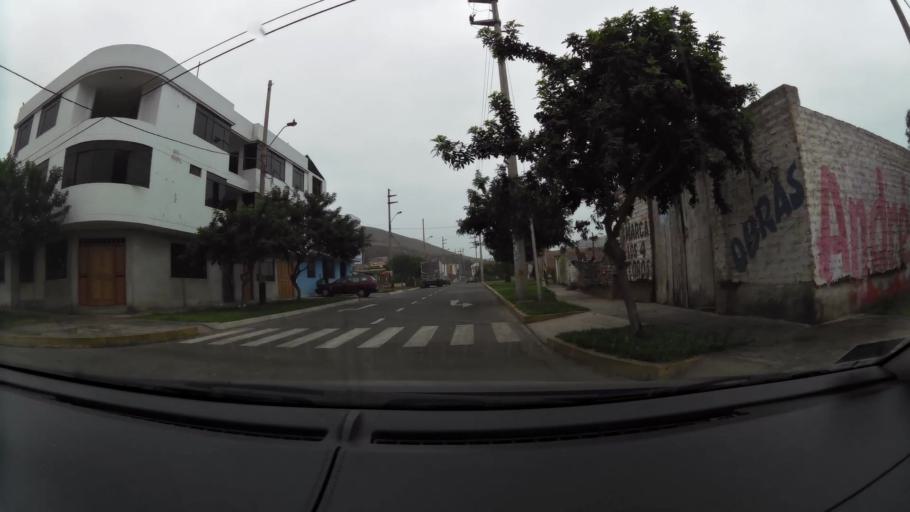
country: PE
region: Lima
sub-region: Provincia de Huaral
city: Chancay
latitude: -11.5861
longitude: -77.2715
